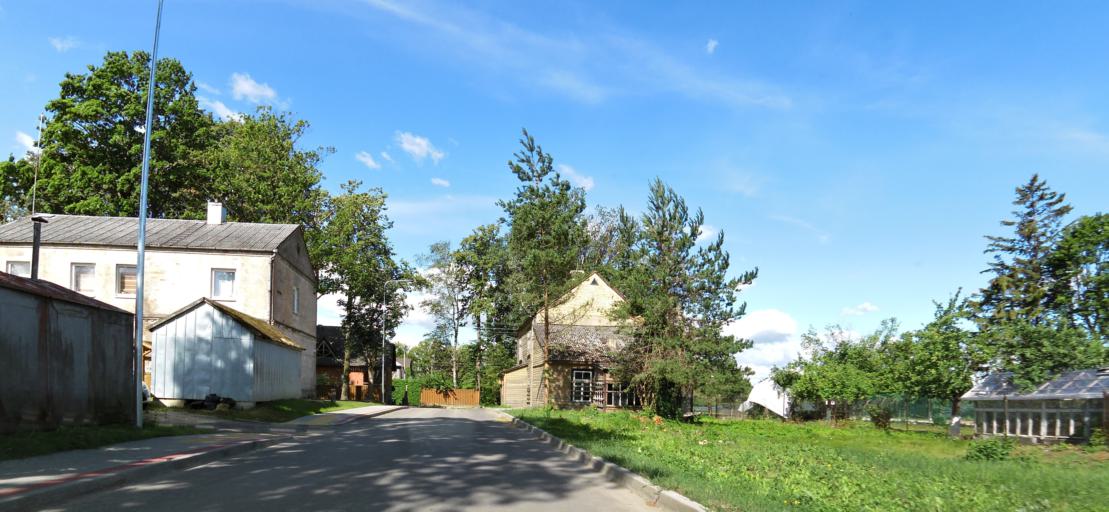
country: LT
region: Panevezys
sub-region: Birzai
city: Birzai
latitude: 56.2030
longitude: 24.7479
